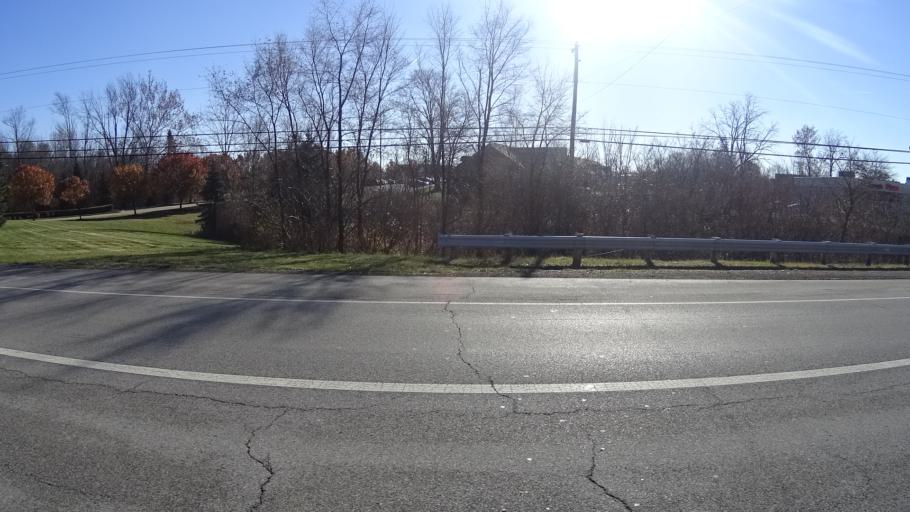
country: US
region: Ohio
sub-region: Lorain County
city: Sheffield
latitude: 41.4271
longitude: -82.0752
